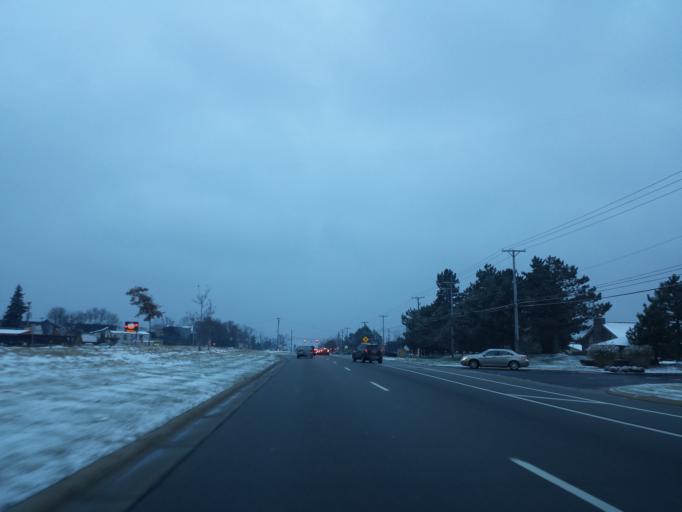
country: US
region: Michigan
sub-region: Oakland County
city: Franklin
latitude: 42.5206
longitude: -83.3430
